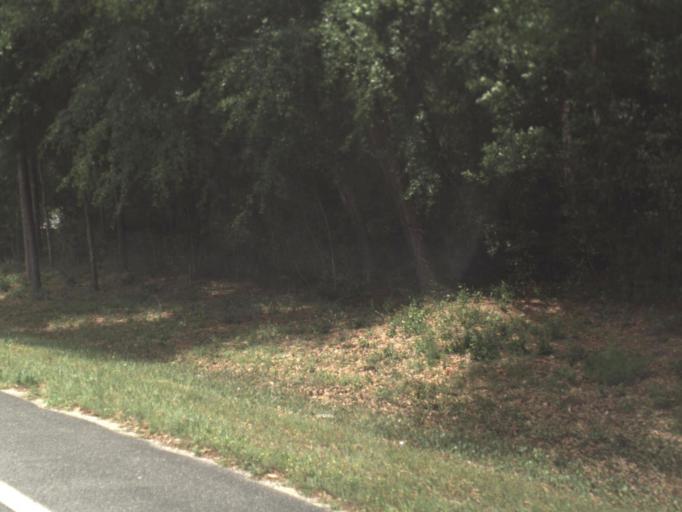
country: US
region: Florida
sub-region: Santa Rosa County
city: Point Baker
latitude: 30.6918
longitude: -87.0558
